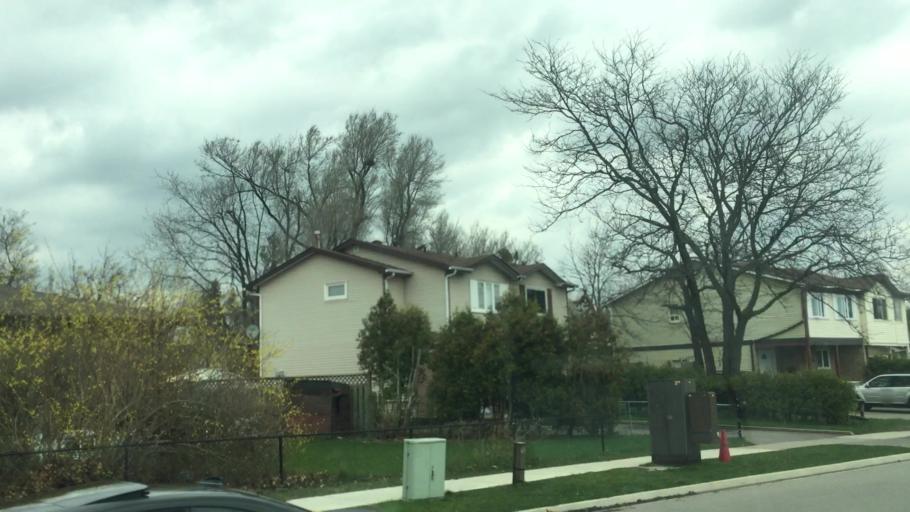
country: CA
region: Ontario
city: Brampton
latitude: 43.7045
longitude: -79.7474
